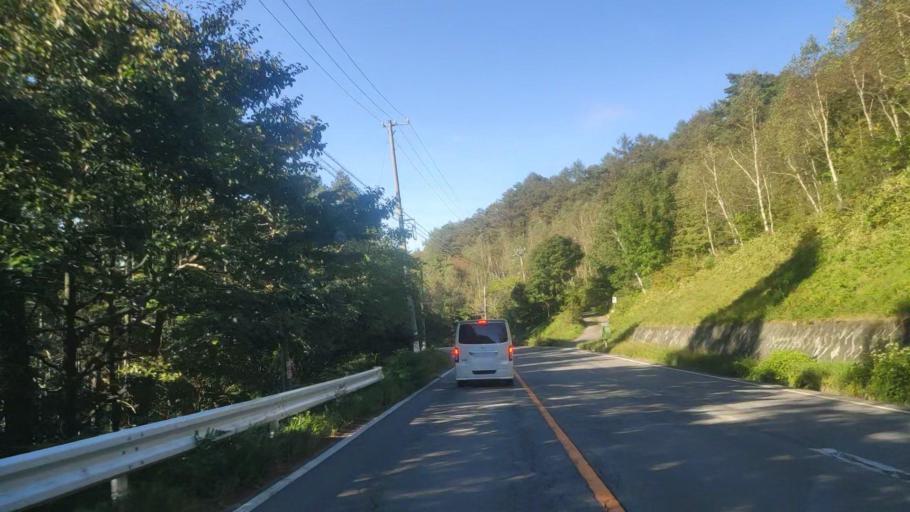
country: JP
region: Nagano
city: Kamimaruko
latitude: 36.1744
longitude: 138.2813
